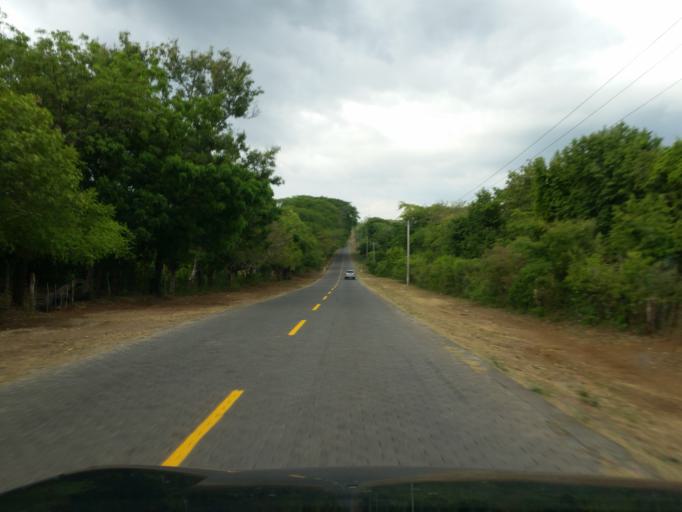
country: NI
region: Managua
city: San Rafael del Sur
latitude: 11.8849
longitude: -86.5145
